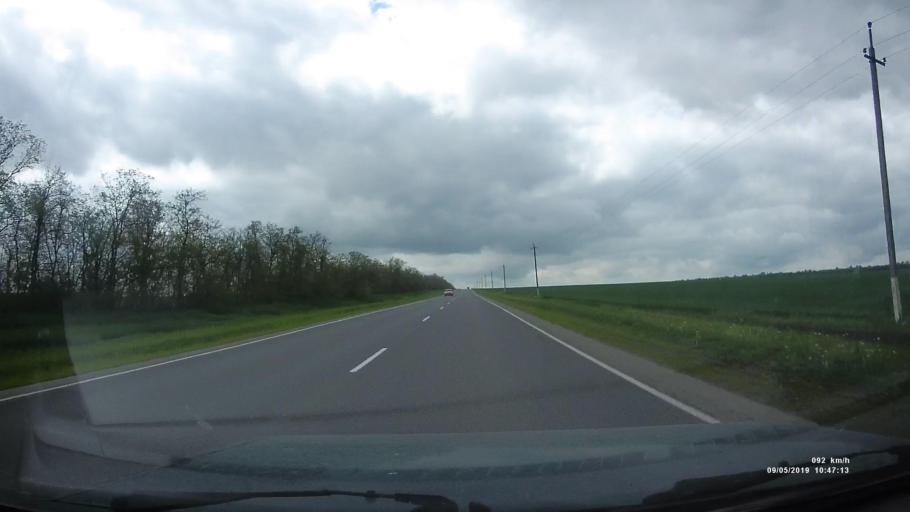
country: RU
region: Rostov
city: Peshkovo
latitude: 46.9738
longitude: 39.3556
